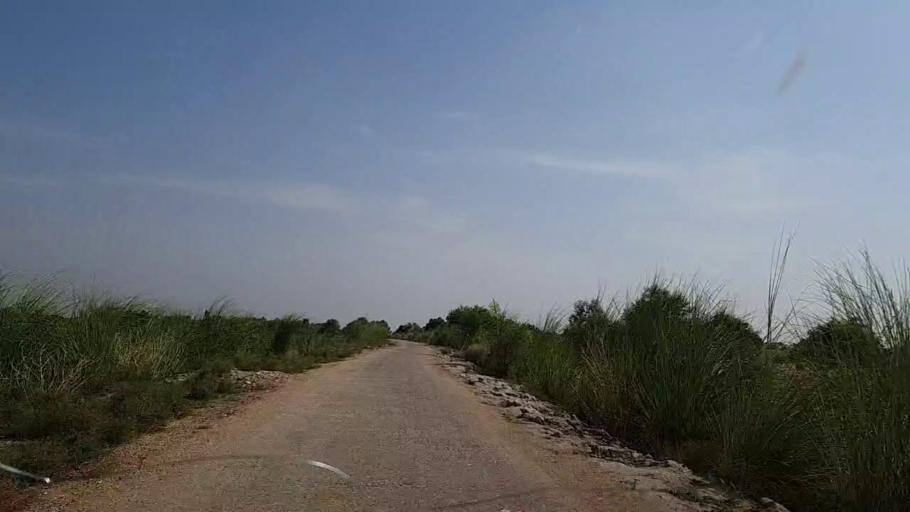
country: PK
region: Sindh
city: Khanpur
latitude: 27.7146
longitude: 69.3623
